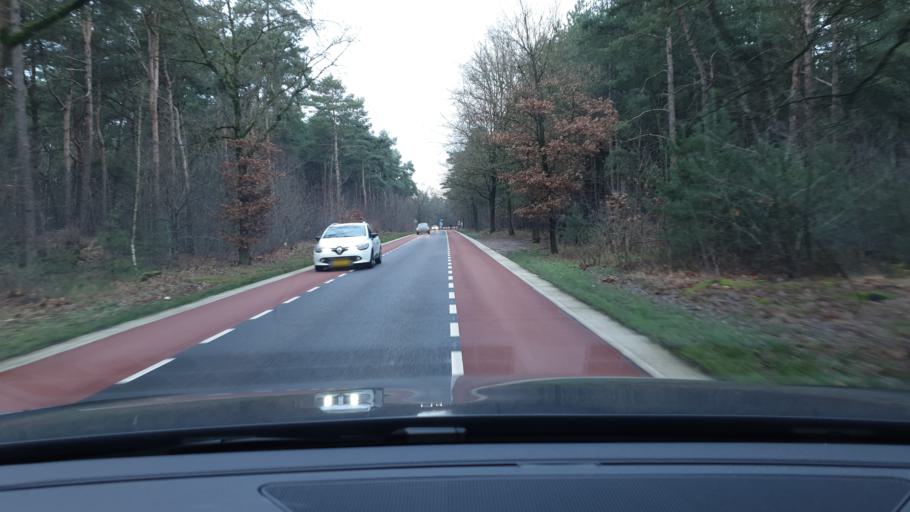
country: NL
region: North Brabant
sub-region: Gemeente Son en Breugel
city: Son
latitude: 51.5117
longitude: 5.4518
